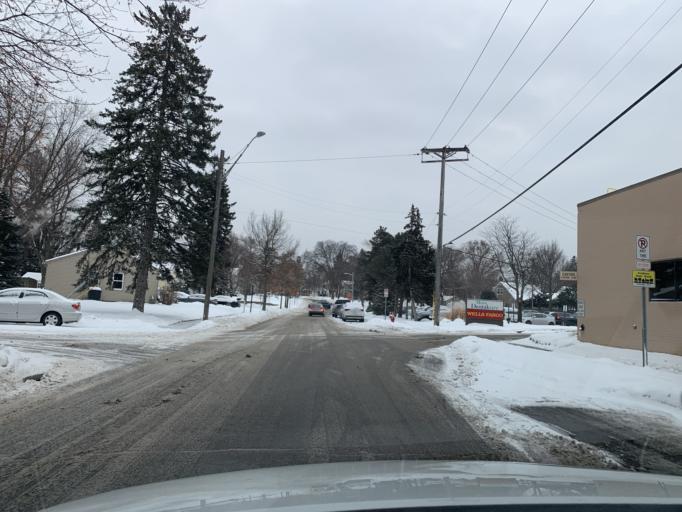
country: US
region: Minnesota
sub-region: Hennepin County
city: Saint Louis Park
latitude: 44.9316
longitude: -93.3432
